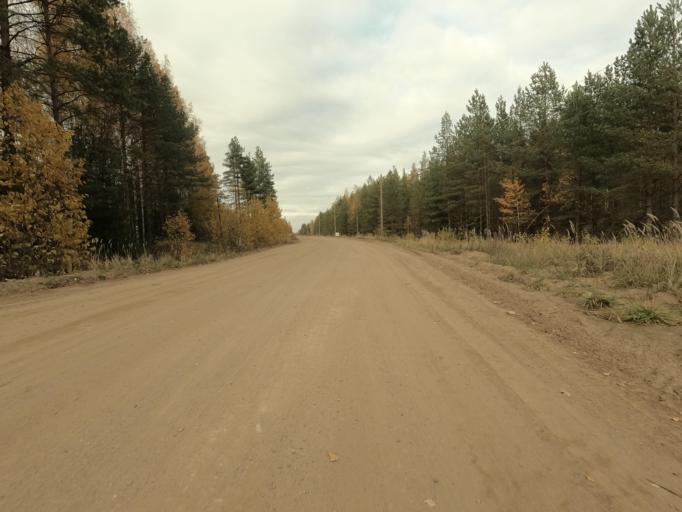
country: RU
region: Leningrad
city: Priladozhskiy
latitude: 59.6891
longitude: 31.3604
